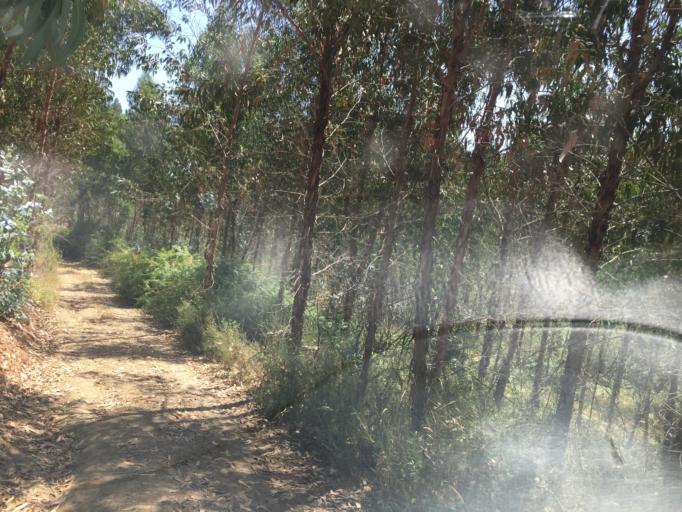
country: PT
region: Santarem
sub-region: Ferreira do Zezere
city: Ferreira do Zezere
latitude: 39.6505
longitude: -8.3167
